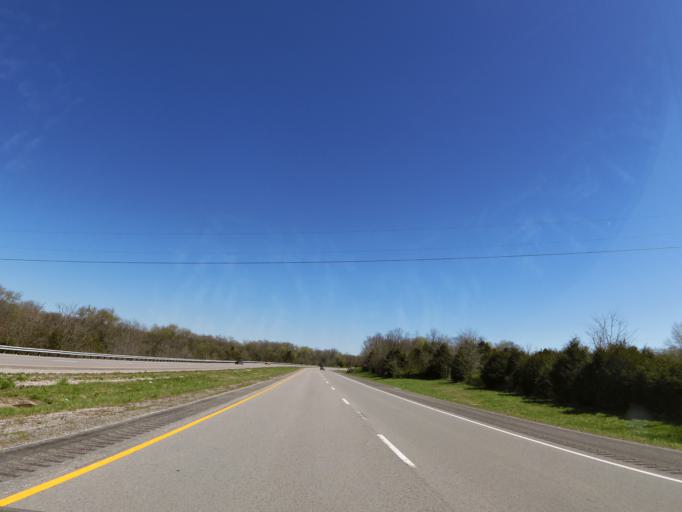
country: US
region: Kentucky
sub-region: Logan County
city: Auburn
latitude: 36.8424
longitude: -86.7901
